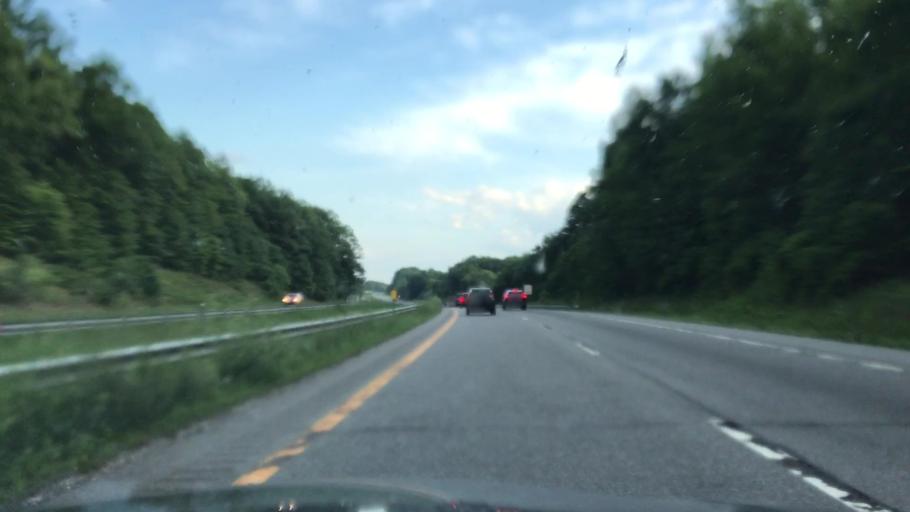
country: US
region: New York
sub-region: Sullivan County
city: Wurtsboro
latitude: 41.5438
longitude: -74.4249
